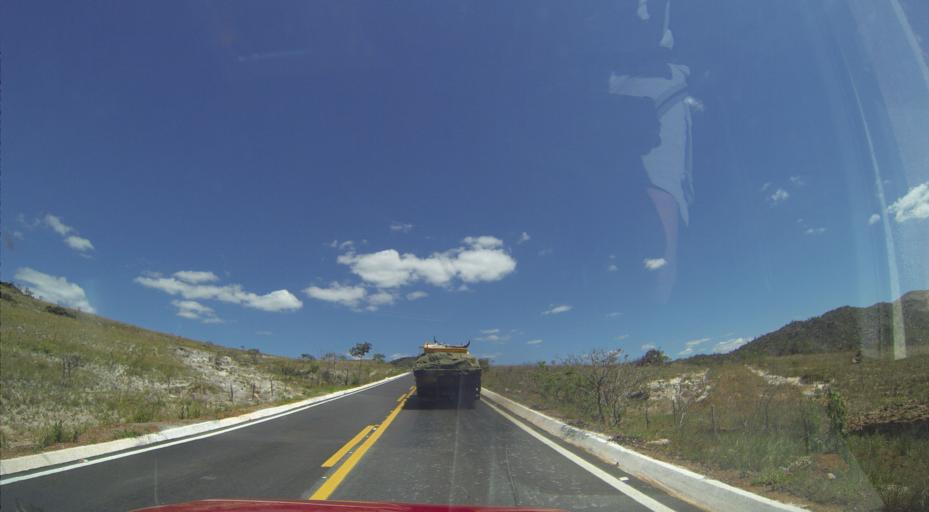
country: BR
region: Minas Gerais
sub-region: Conceicao Do Mato Dentro
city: Conceicao do Mato Dentro
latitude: -19.2825
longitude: -43.5805
